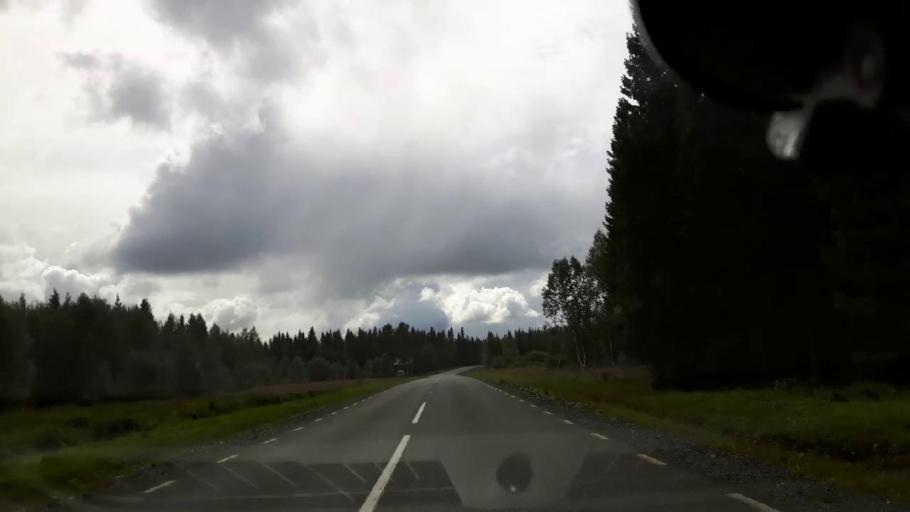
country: SE
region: Jaemtland
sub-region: Krokoms Kommun
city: Valla
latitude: 63.4801
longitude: 13.8560
